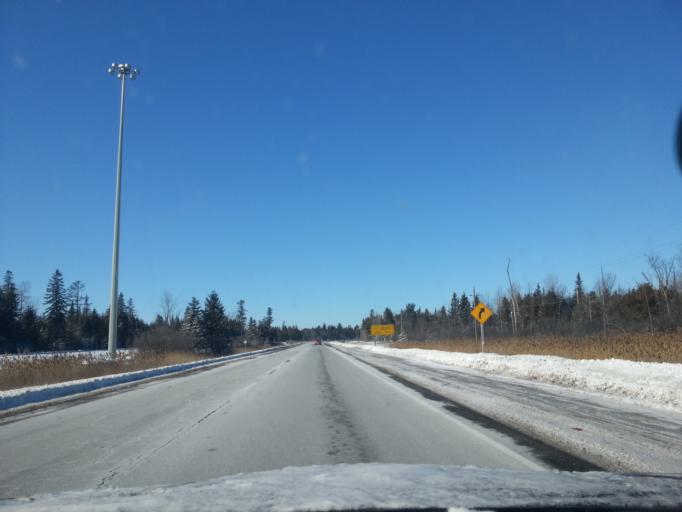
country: CA
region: Ontario
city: Bells Corners
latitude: 45.2723
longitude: -75.9810
